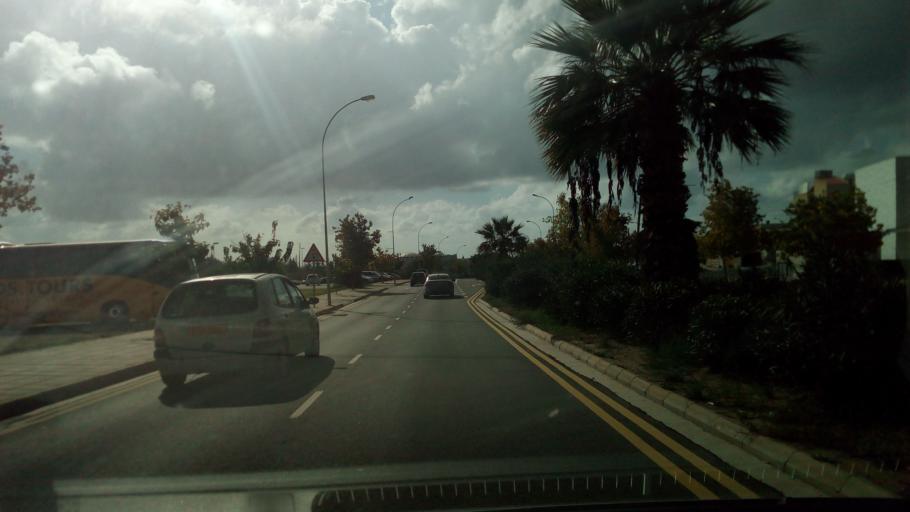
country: CY
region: Pafos
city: Paphos
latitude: 34.7711
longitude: 32.4422
